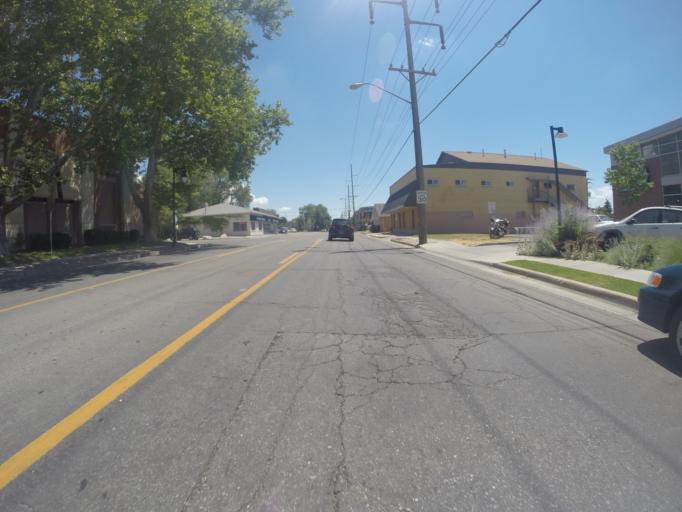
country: US
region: Utah
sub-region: Salt Lake County
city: South Salt Lake
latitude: 40.7242
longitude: -111.8654
